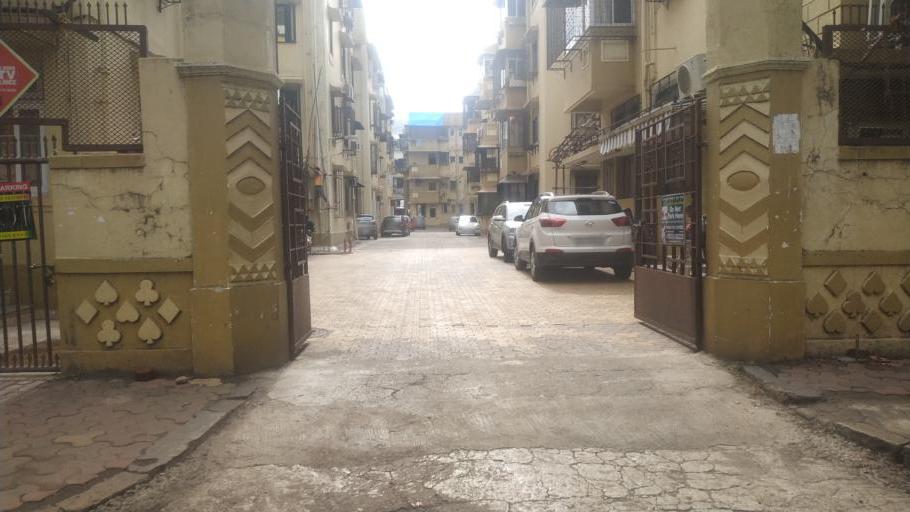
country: IN
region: Maharashtra
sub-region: Mumbai Suburban
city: Mumbai
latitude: 19.0276
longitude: 72.8436
